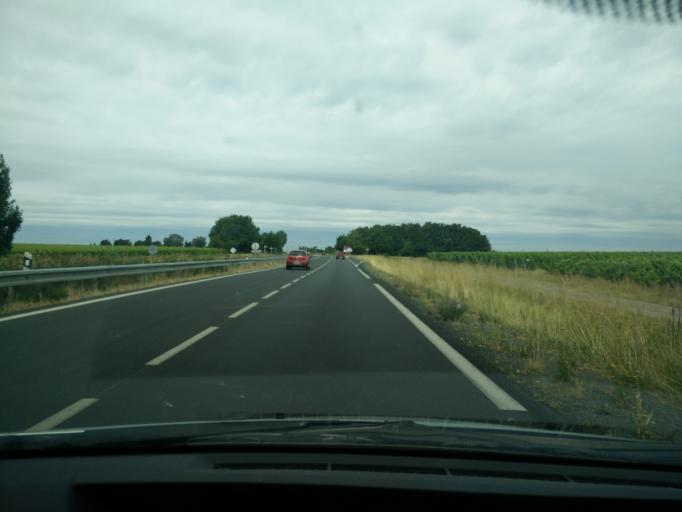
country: FR
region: Pays de la Loire
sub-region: Departement de Maine-et-Loire
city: Juigne-sur-Loire
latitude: 47.3842
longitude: -0.4826
